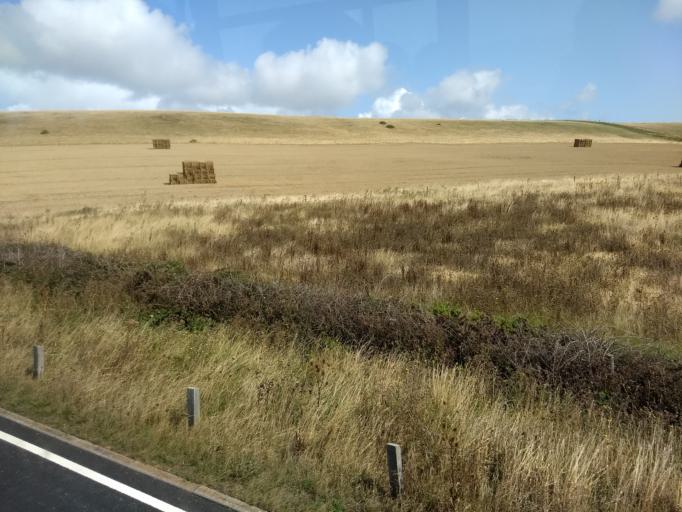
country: GB
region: England
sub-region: Isle of Wight
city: Freshwater
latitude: 50.6592
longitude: -1.4695
